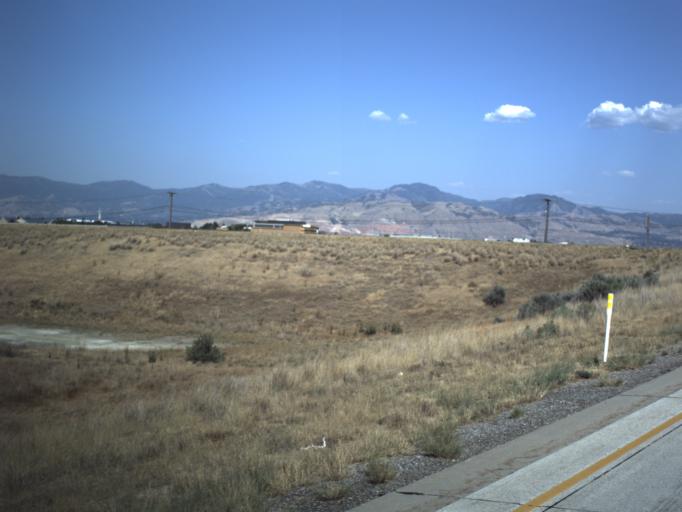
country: US
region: Utah
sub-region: Salt Lake County
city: West Valley City
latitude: 40.7692
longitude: -112.0265
